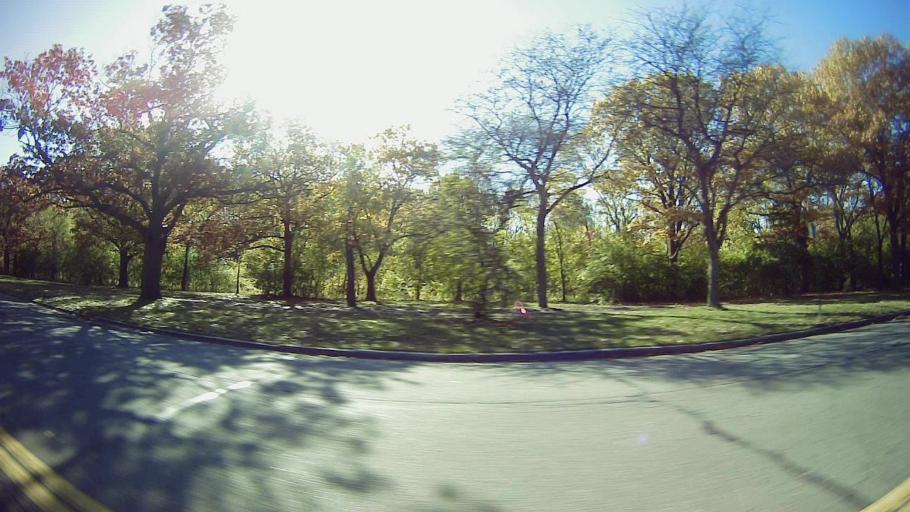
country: US
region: Michigan
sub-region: Wayne County
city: Dearborn Heights
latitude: 42.3684
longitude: -83.2502
